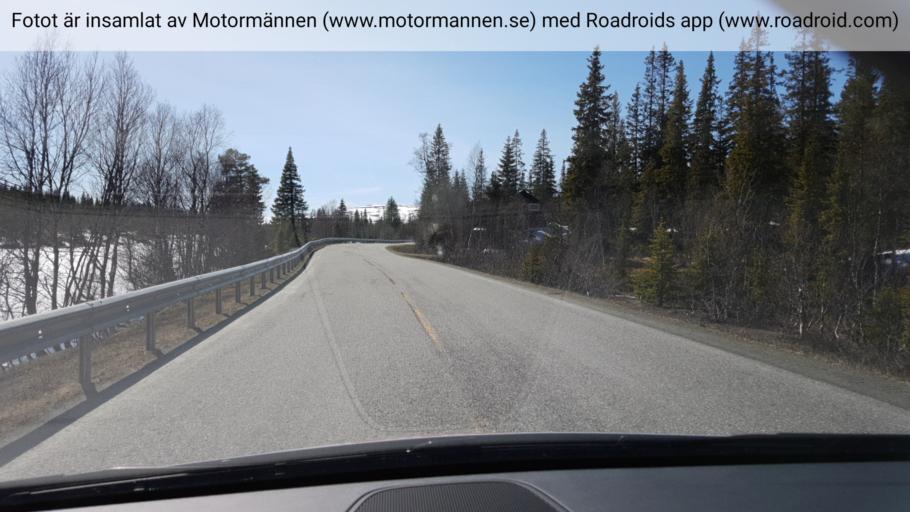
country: NO
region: Nord-Trondelag
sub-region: Snasa
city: Snaase
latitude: 63.6850
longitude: 12.2877
